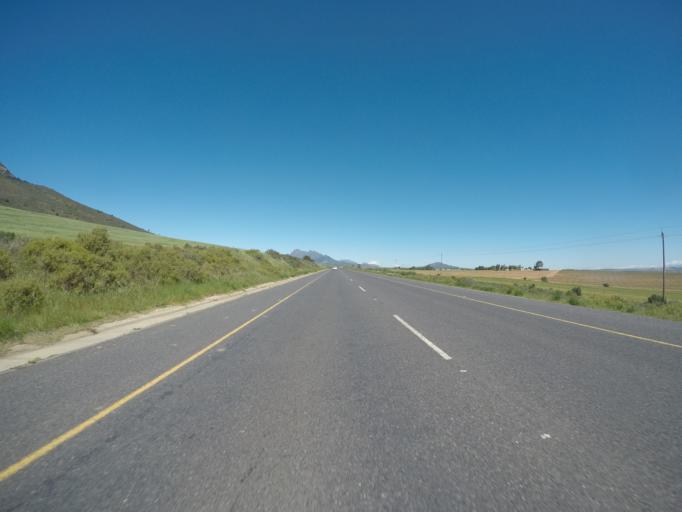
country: ZA
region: Western Cape
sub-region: Cape Winelands District Municipality
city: Noorder-Paarl
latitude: -33.7311
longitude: 18.8910
